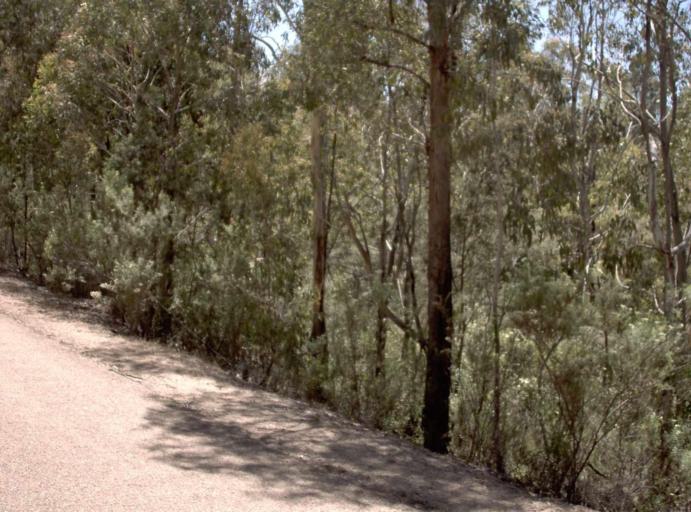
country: AU
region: New South Wales
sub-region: Snowy River
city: Jindabyne
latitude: -37.0490
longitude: 148.2760
